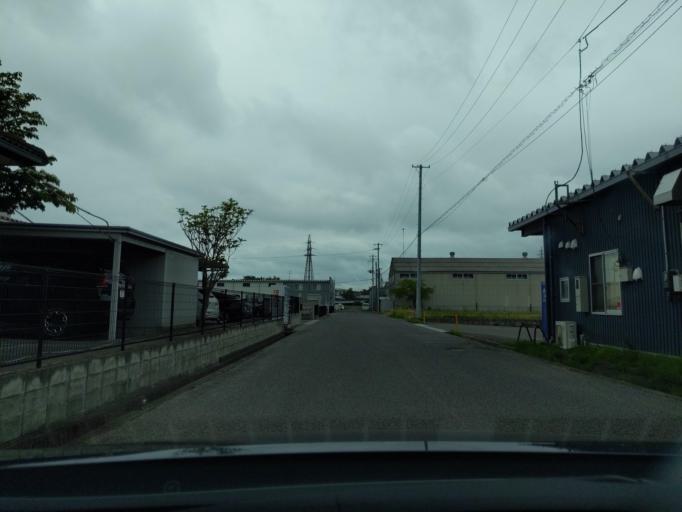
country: JP
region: Fukushima
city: Koriyama
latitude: 37.3596
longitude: 140.3453
